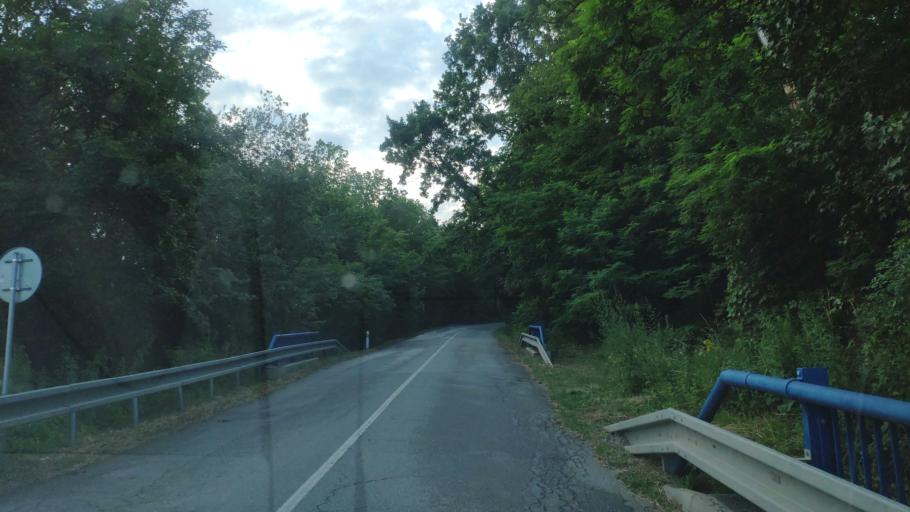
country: SK
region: Kosicky
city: Moldava nad Bodvou
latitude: 48.6893
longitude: 20.9746
